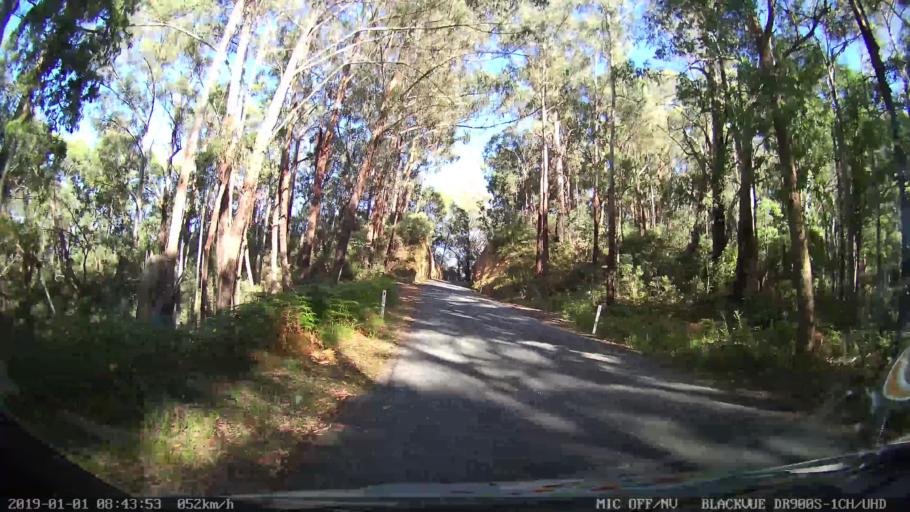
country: AU
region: New South Wales
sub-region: Snowy River
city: Jindabyne
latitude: -36.3141
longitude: 148.1915
